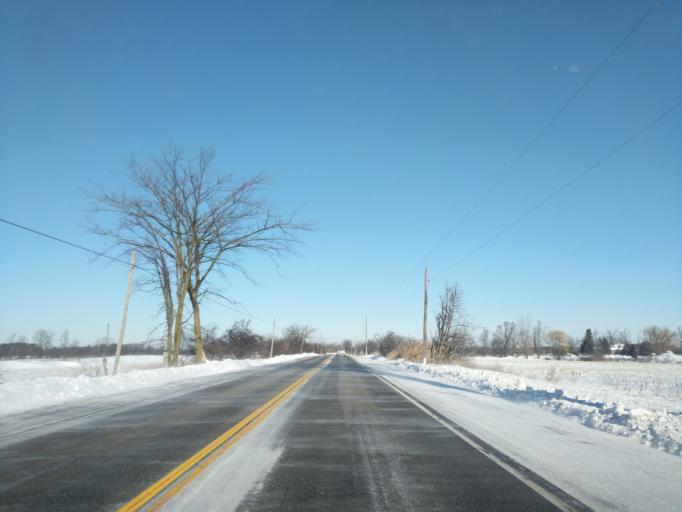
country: CA
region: Ontario
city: Pickering
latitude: 43.8620
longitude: -79.1340
